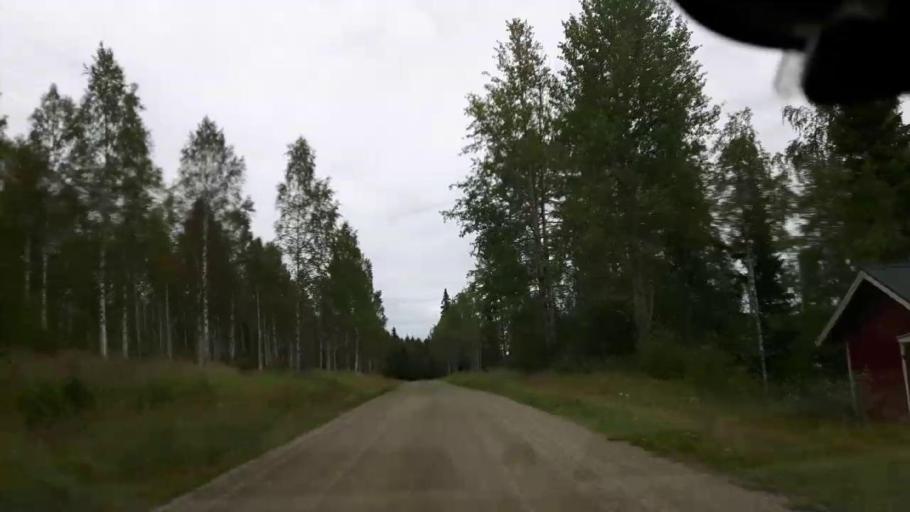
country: SE
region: Jaemtland
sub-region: Braecke Kommun
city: Braecke
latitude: 62.9875
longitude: 15.3876
